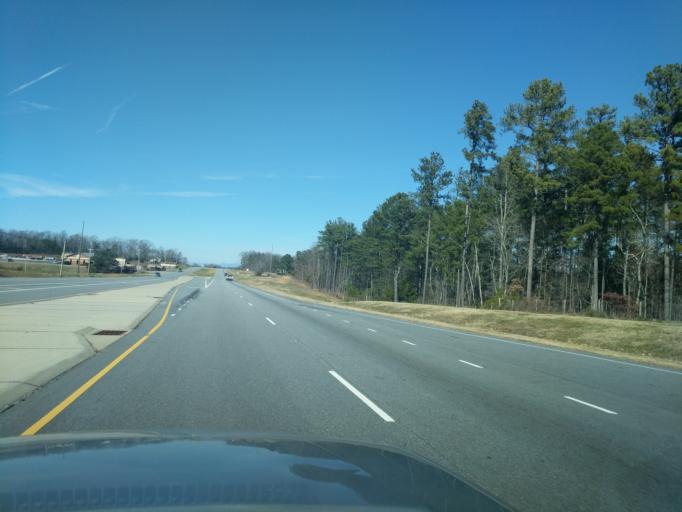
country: US
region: North Carolina
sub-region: Rutherford County
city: Forest City
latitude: 35.2592
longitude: -81.8816
